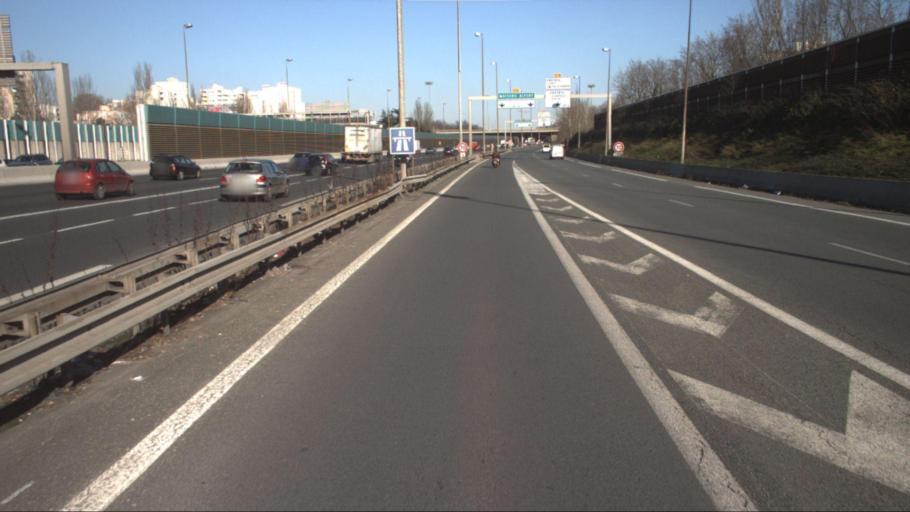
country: FR
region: Ile-de-France
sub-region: Departement du Val-de-Marne
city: Maisons-Alfort
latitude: 48.7960
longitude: 2.4433
